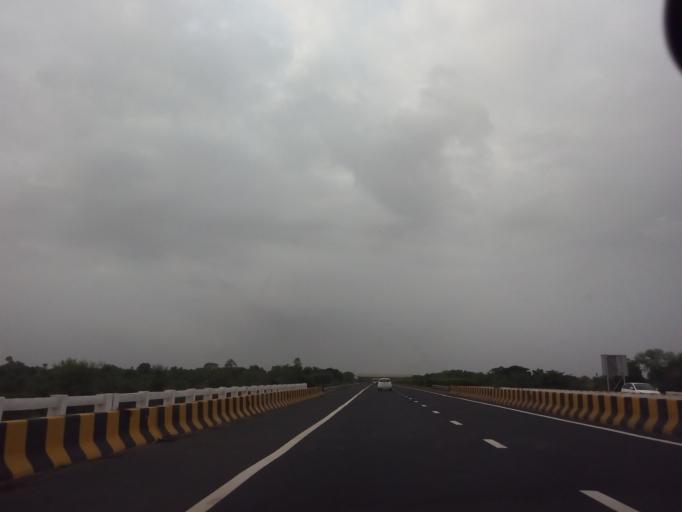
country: IN
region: Gujarat
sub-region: Kheda
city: Mahemdavad
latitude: 22.8707
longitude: 72.8026
